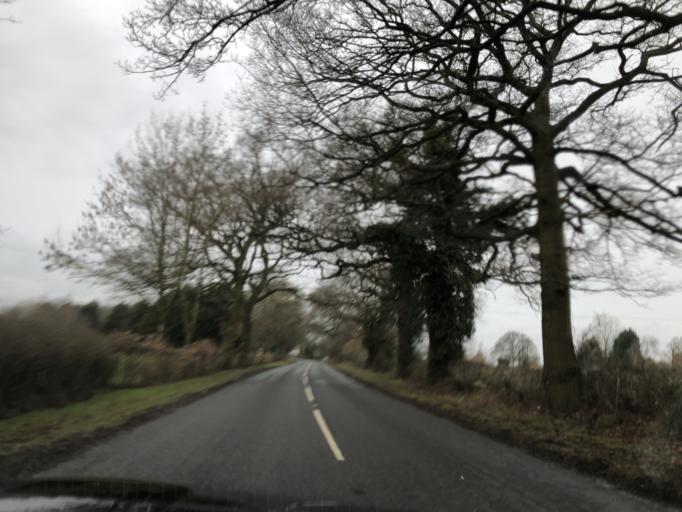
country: GB
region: England
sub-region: Warwickshire
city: Wroxall
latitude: 52.2916
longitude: -1.7070
